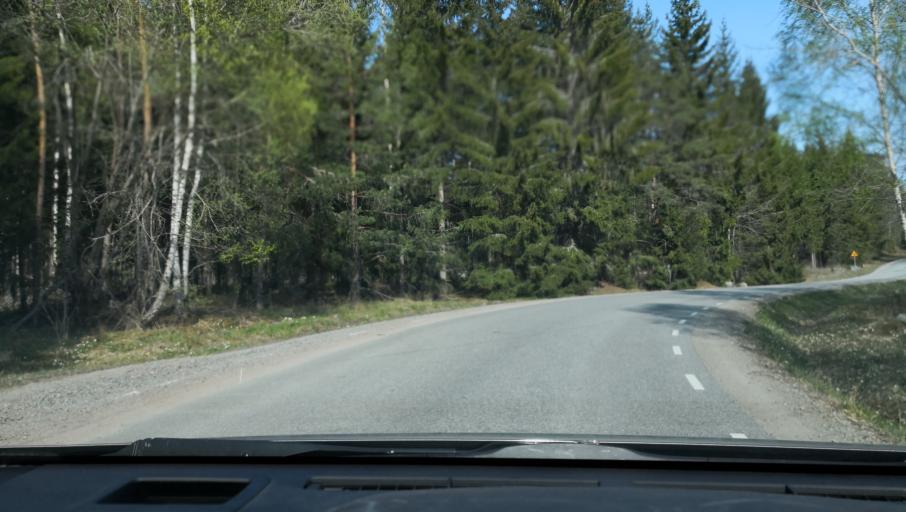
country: SE
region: Vaestmanland
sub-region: Sala Kommun
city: Sala
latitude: 59.9973
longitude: 16.6540
